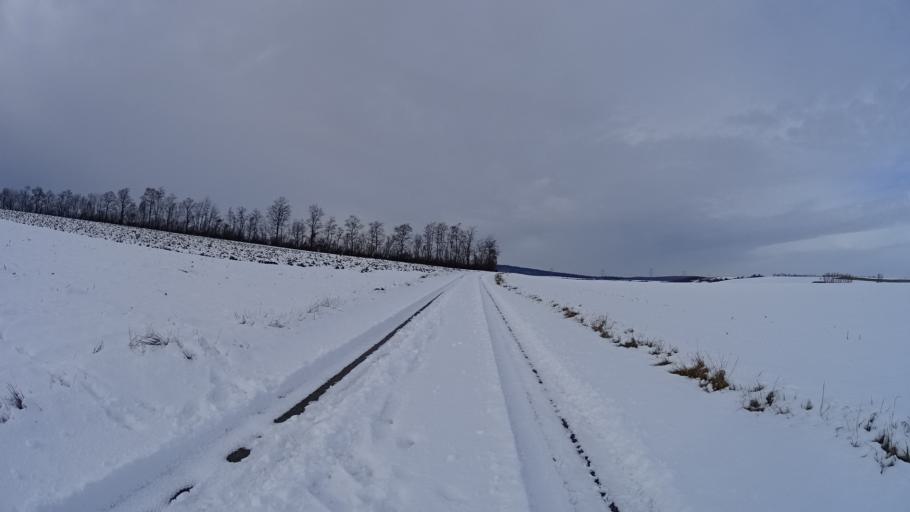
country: AT
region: Lower Austria
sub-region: Politischer Bezirk Korneuburg
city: Harmannsdorf
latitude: 48.3885
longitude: 16.3562
